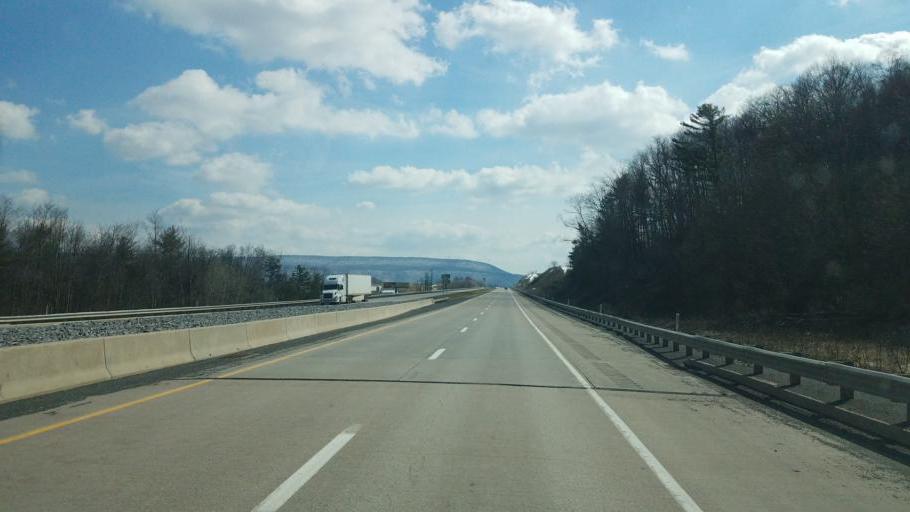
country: US
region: Pennsylvania
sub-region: Mifflin County
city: Milroy
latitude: 40.7178
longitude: -77.6013
